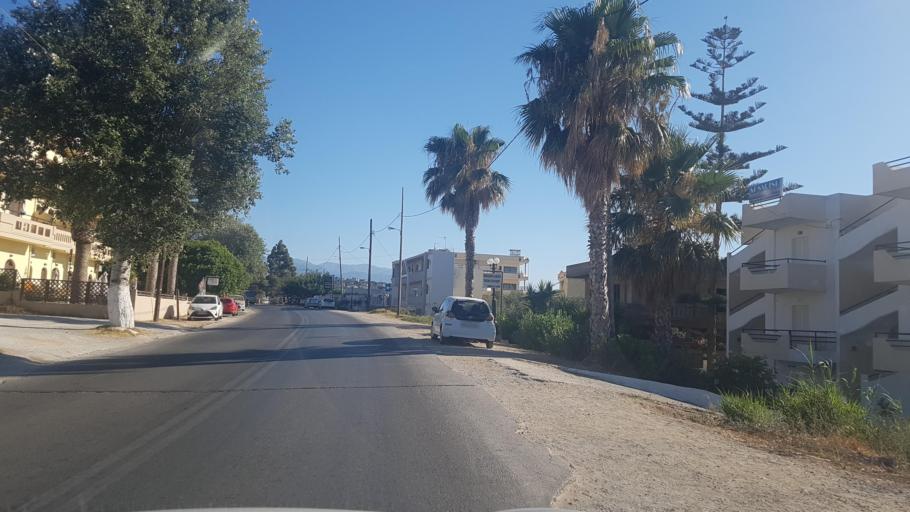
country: GR
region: Crete
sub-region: Nomos Chanias
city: Daratsos
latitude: 35.5109
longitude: 23.9824
